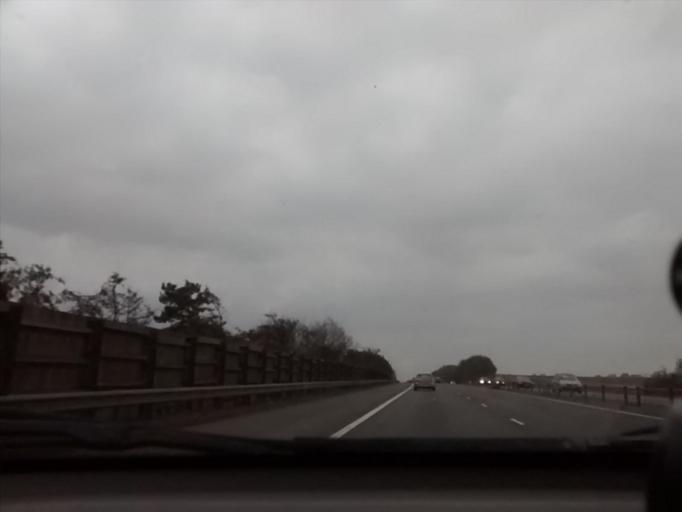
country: GB
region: England
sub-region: Essex
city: Saffron Walden
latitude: 51.9988
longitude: 0.1949
